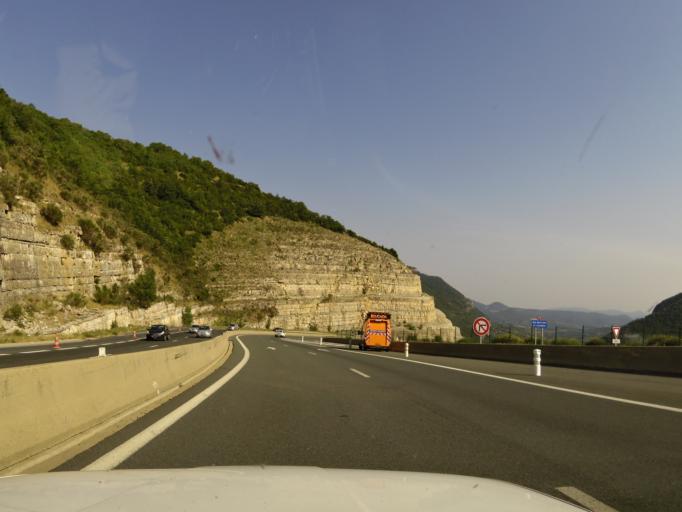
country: FR
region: Languedoc-Roussillon
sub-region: Departement de l'Herault
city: Lodeve
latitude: 43.8155
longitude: 3.3188
